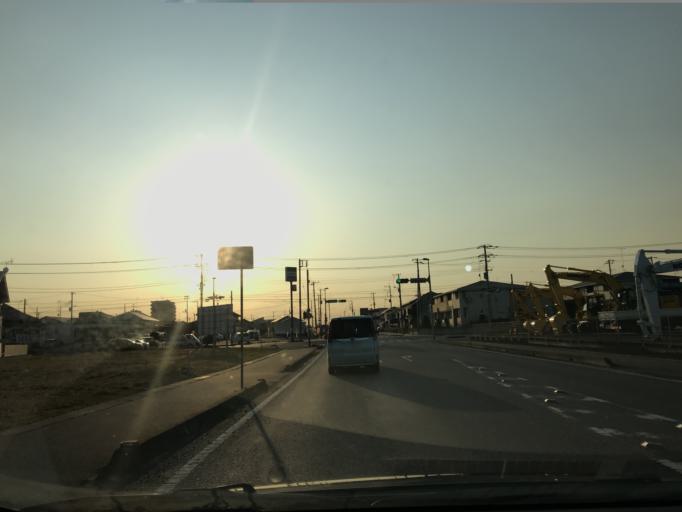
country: JP
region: Ibaraki
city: Mitsukaido
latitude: 36.0001
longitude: 140.0466
